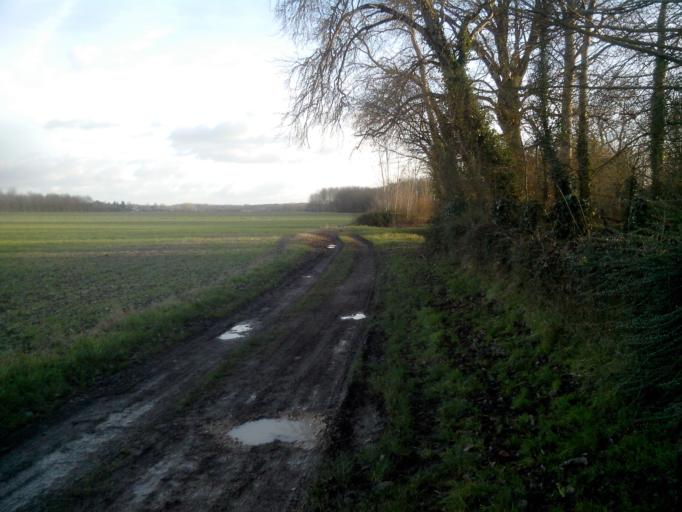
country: FR
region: Centre
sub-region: Departement du Loir-et-Cher
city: Villiers-sur-Loir
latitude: 47.7992
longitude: 0.9833
